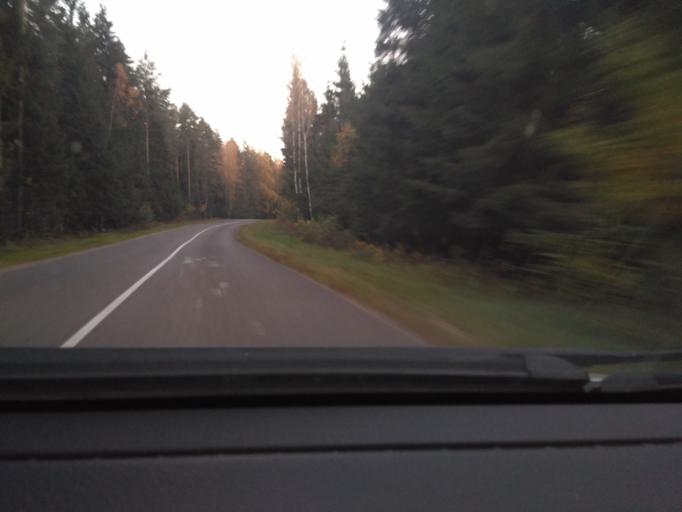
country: BY
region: Minsk
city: Loshnitsa
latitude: 54.3732
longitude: 28.6240
